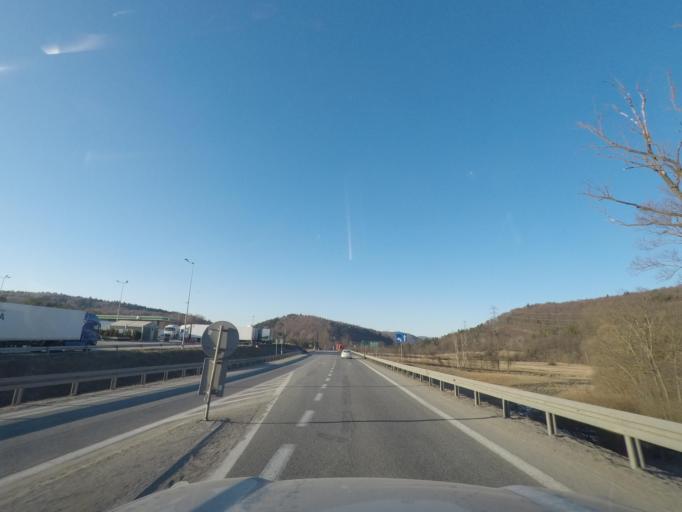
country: PL
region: Subcarpathian Voivodeship
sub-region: Powiat krosnienski
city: Jasliska
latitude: 49.4385
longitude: 21.6908
